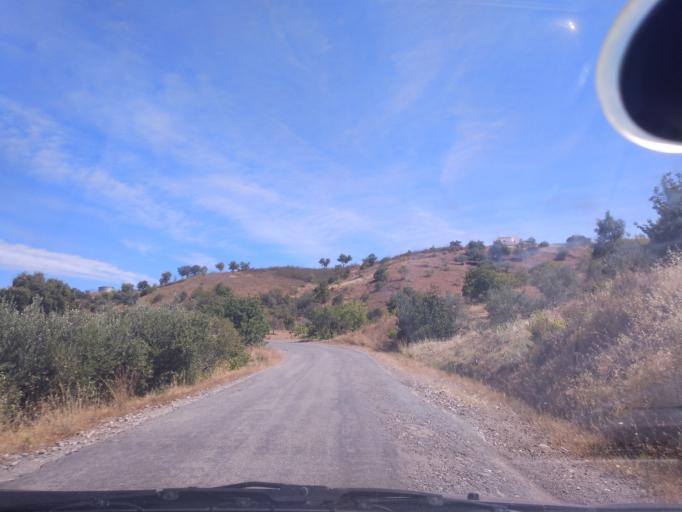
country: PT
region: Faro
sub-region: Olhao
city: Moncarapacho
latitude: 37.1697
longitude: -7.8038
